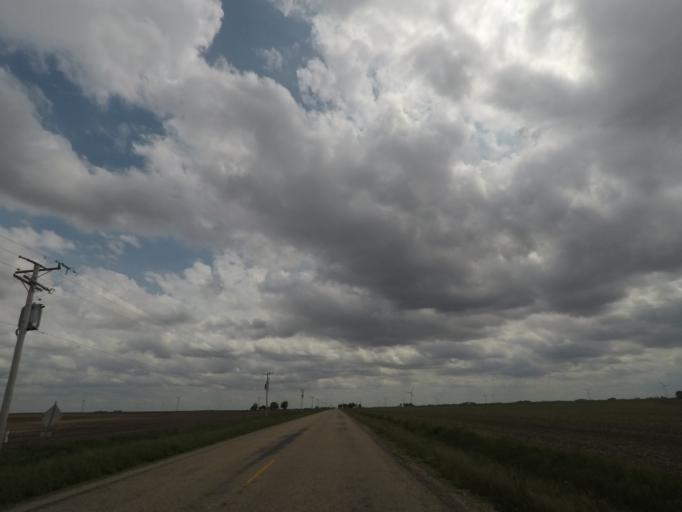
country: US
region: Illinois
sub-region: Macon County
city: Maroa
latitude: 40.0702
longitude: -89.0860
